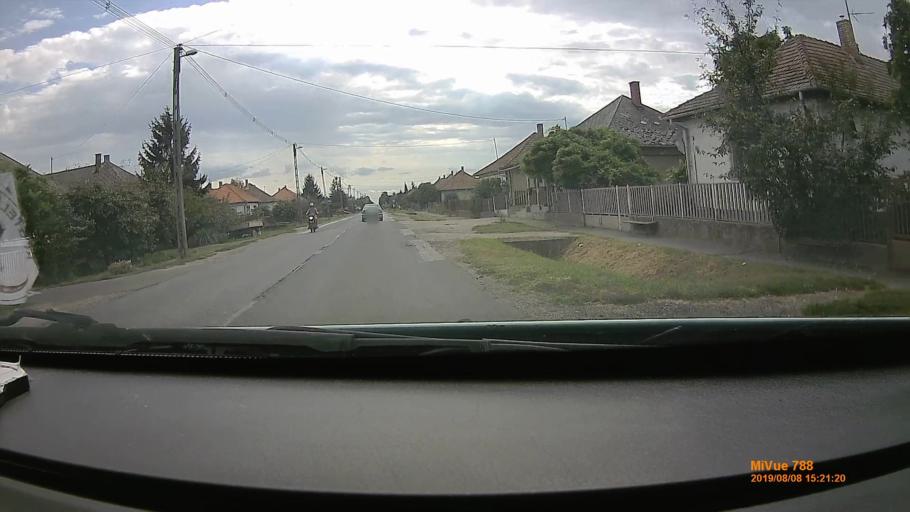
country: HU
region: Szabolcs-Szatmar-Bereg
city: Tunyogmatolcs
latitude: 47.9664
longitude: 22.4489
